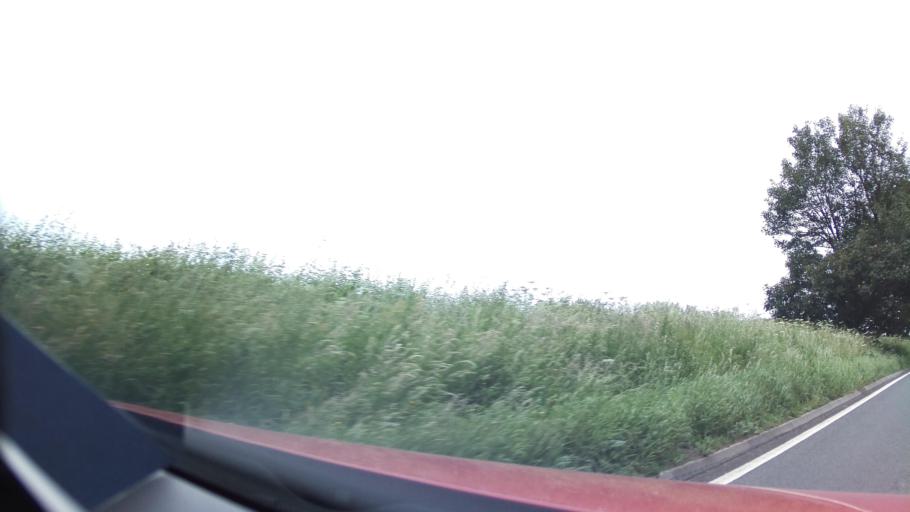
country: GB
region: England
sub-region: Staffordshire
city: Mayfield
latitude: 52.9873
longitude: -1.7467
